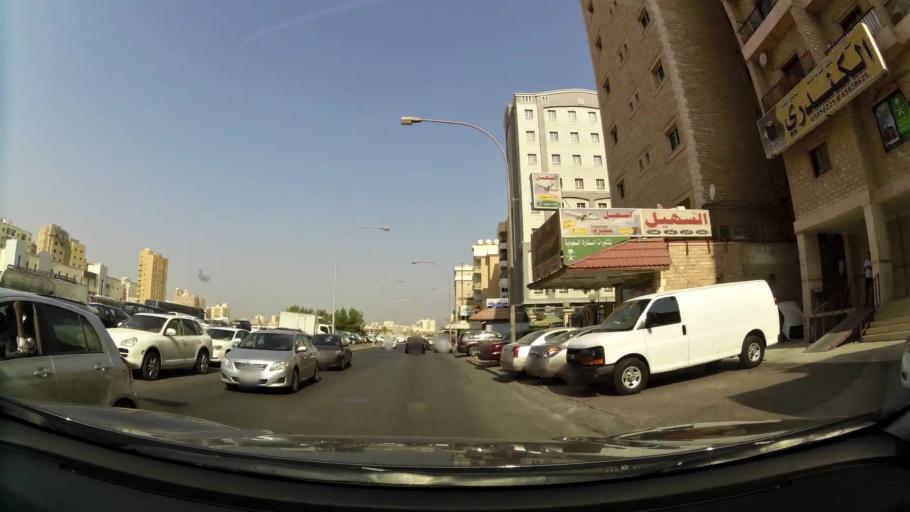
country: KW
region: Muhafazat Hawalli
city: Hawalli
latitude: 29.3296
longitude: 48.0167
